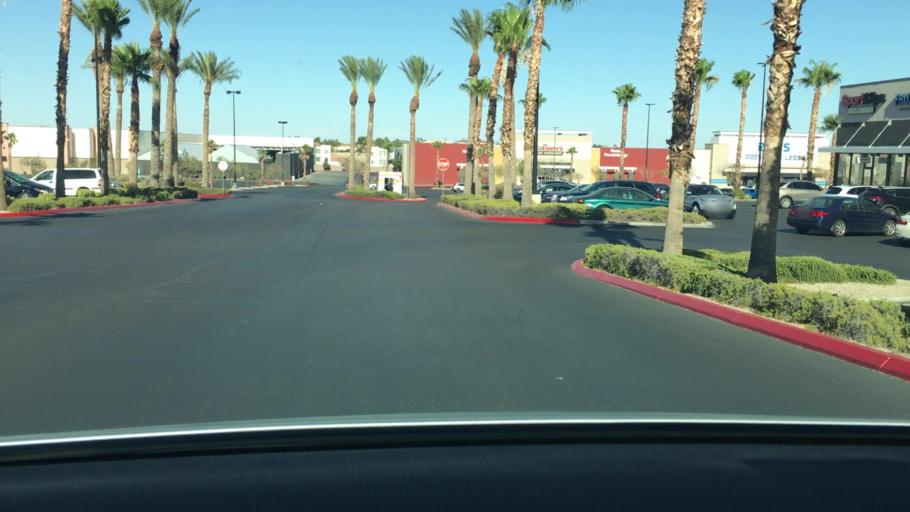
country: US
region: Nevada
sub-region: Clark County
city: Summerlin South
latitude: 36.0963
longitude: -115.2968
